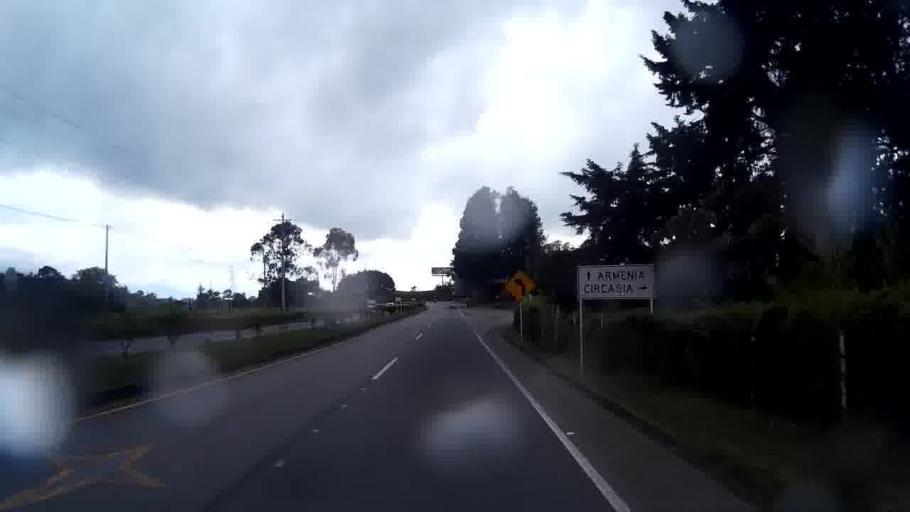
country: CO
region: Quindio
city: Circasia
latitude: 4.6224
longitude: -75.6246
